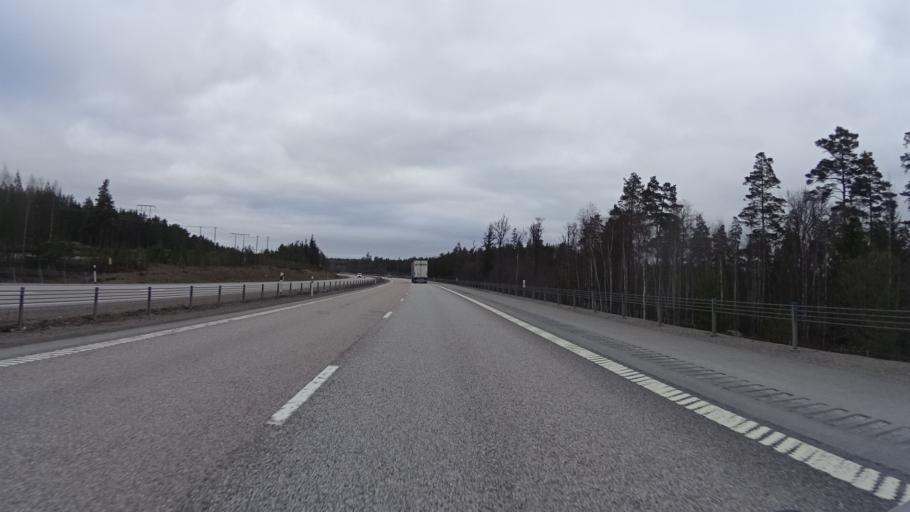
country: SE
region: Soedermanland
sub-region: Strangnas Kommun
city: Strangnas
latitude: 59.3459
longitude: 17.0101
